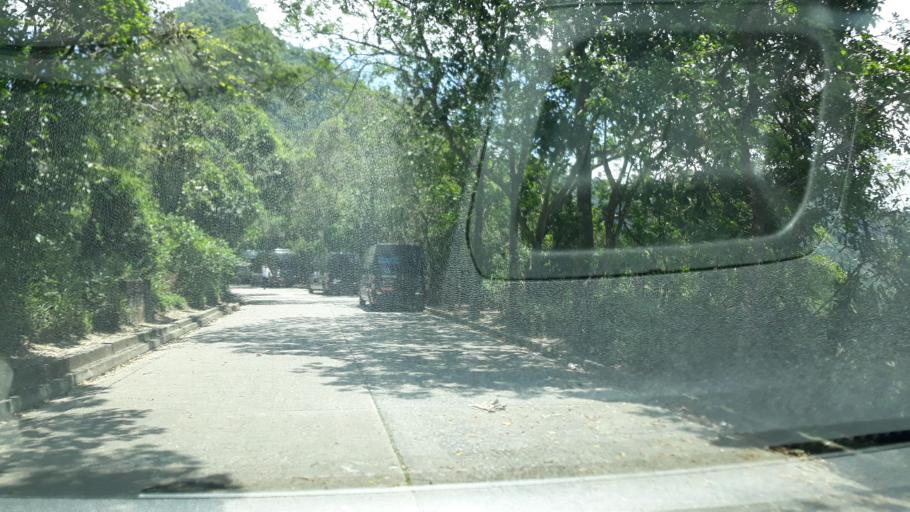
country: BR
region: Rio de Janeiro
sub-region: Rio De Janeiro
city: Rio de Janeiro
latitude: -22.9478
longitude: -43.2008
